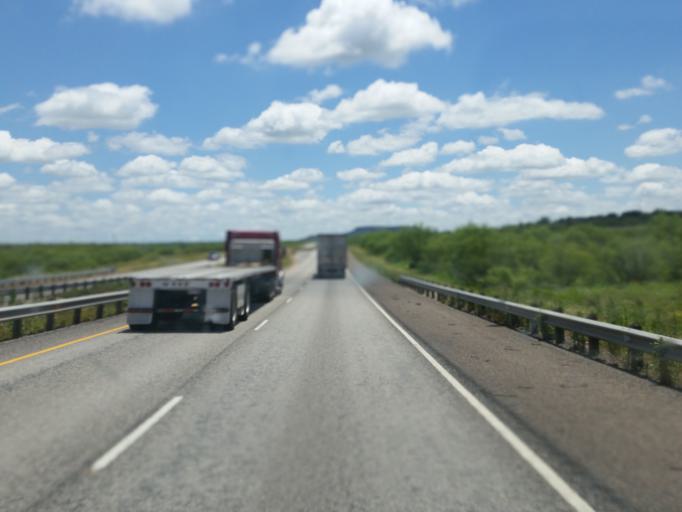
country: US
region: Texas
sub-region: Garza County
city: Post
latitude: 32.9830
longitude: -101.1194
